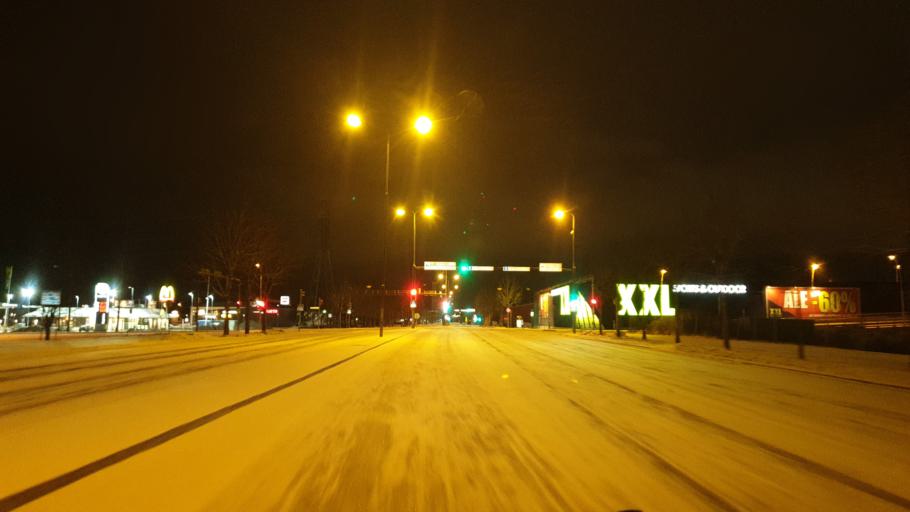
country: FI
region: Northern Ostrobothnia
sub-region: Oulu
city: Oulu
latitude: 64.9956
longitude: 25.4647
